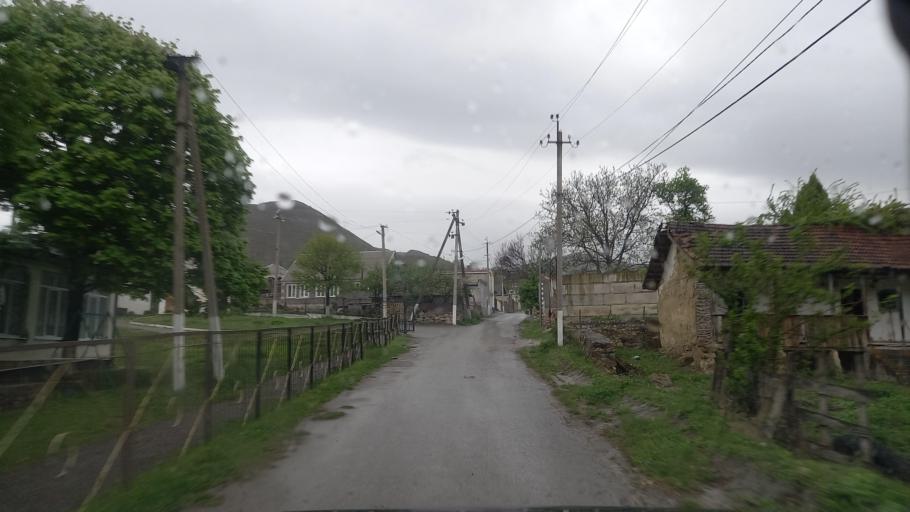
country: RU
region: Kabardino-Balkariya
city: Gundelen
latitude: 43.5984
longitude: 43.1527
